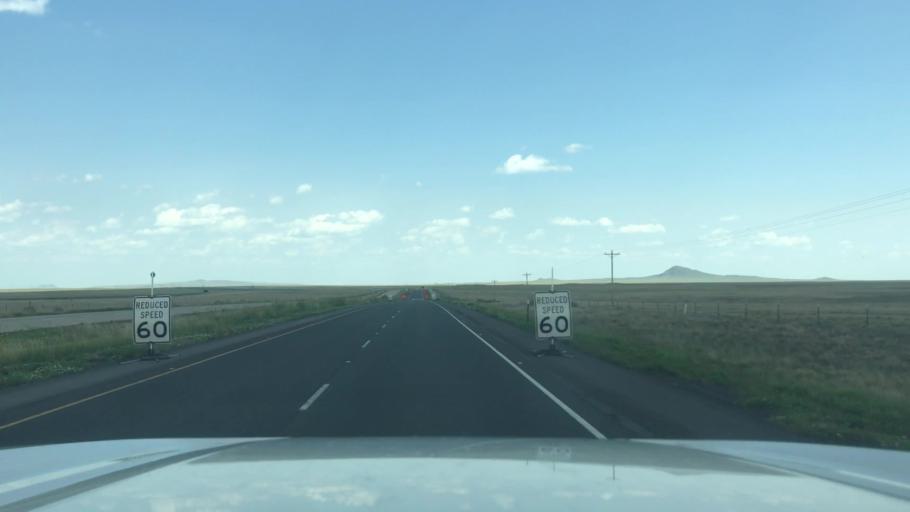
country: US
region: New Mexico
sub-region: Union County
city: Clayton
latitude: 36.6219
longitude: -103.6978
